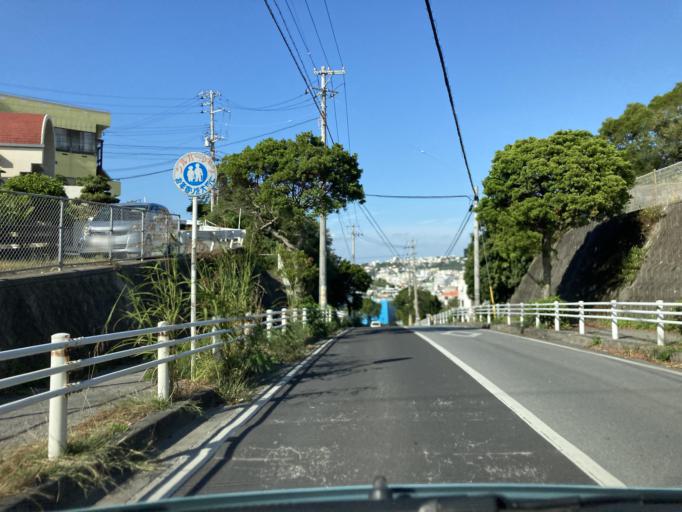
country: JP
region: Okinawa
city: Tomigusuku
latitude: 26.1782
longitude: 127.7062
